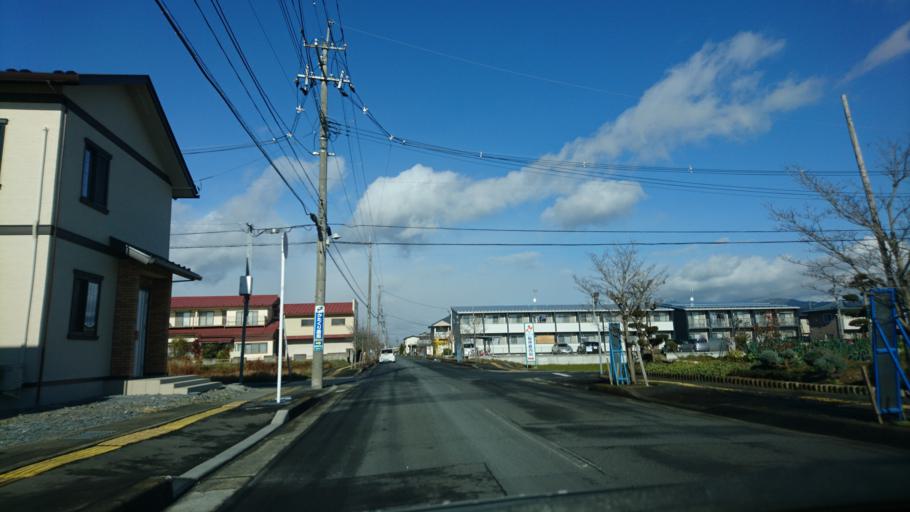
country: JP
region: Iwate
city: Ichinoseki
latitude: 38.9414
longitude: 141.1329
